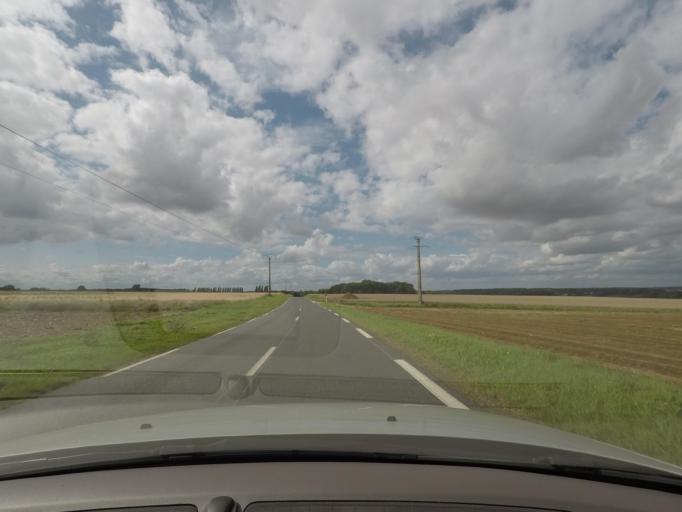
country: FR
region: Haute-Normandie
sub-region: Departement de l'Eure
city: Les Andelys
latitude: 49.2323
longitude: 1.4335
